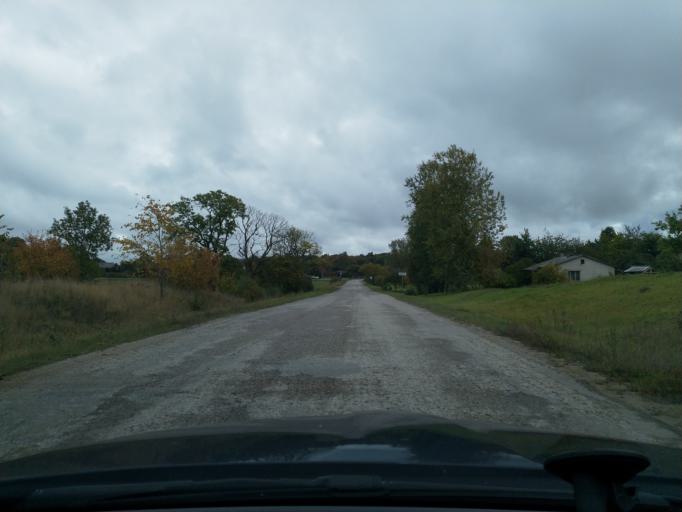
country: LV
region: Alsunga
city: Alsunga
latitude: 57.0232
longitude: 21.6865
